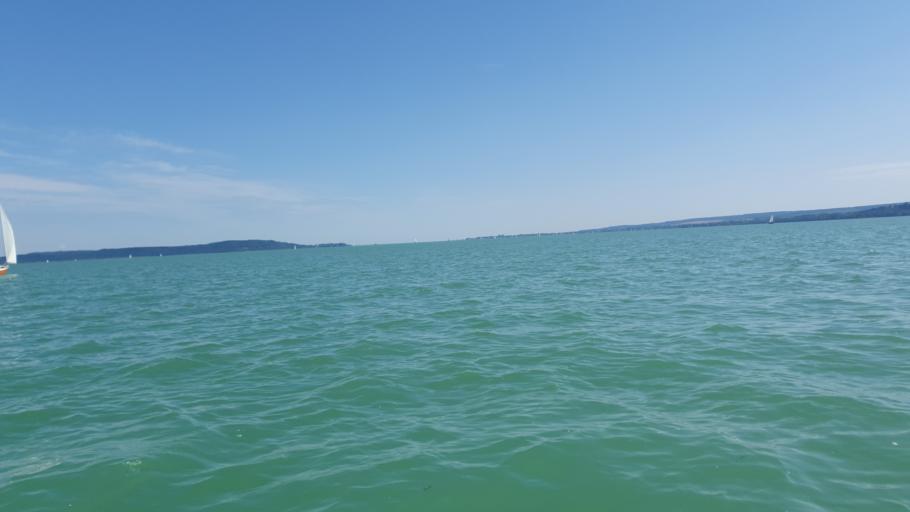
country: HU
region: Somogy
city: Balatonszarszo
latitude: 46.8493
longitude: 17.8168
